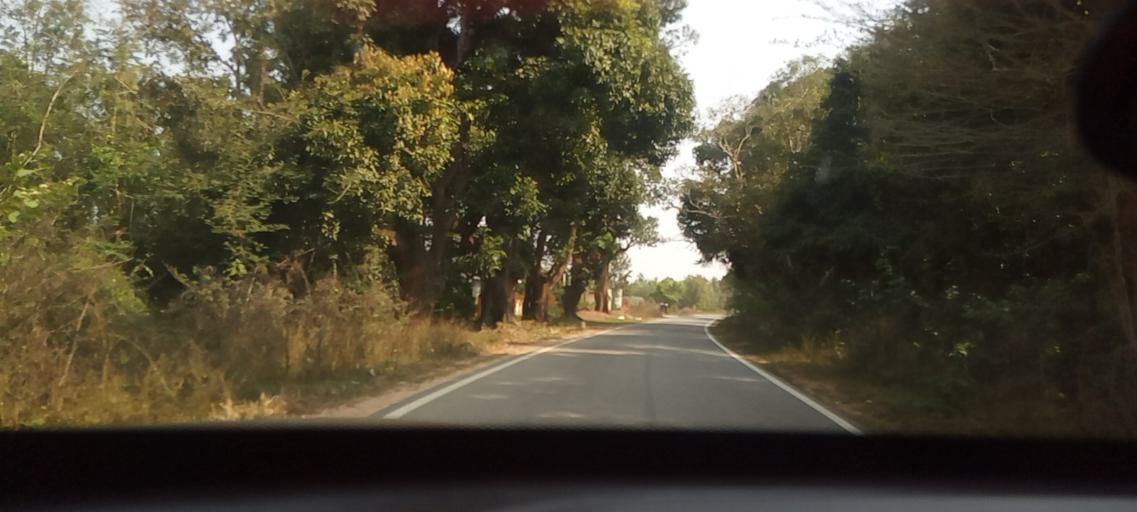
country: IN
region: Karnataka
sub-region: Hassan
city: Belur
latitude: 13.1866
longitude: 75.7997
